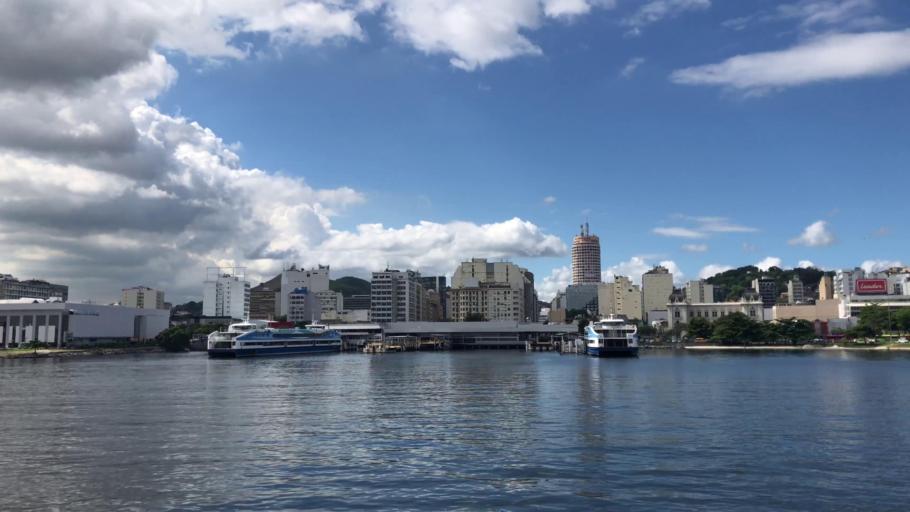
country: BR
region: Rio de Janeiro
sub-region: Niteroi
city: Niteroi
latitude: -22.8920
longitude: -43.1262
